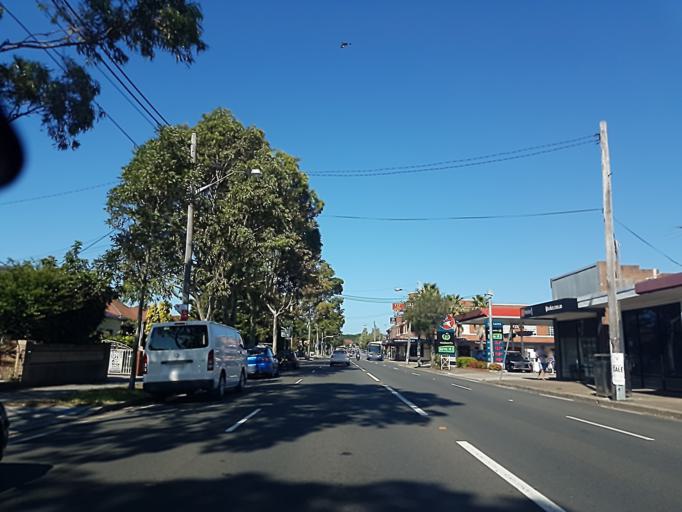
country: AU
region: New South Wales
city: Alexandria
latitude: -33.9227
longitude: 151.2054
